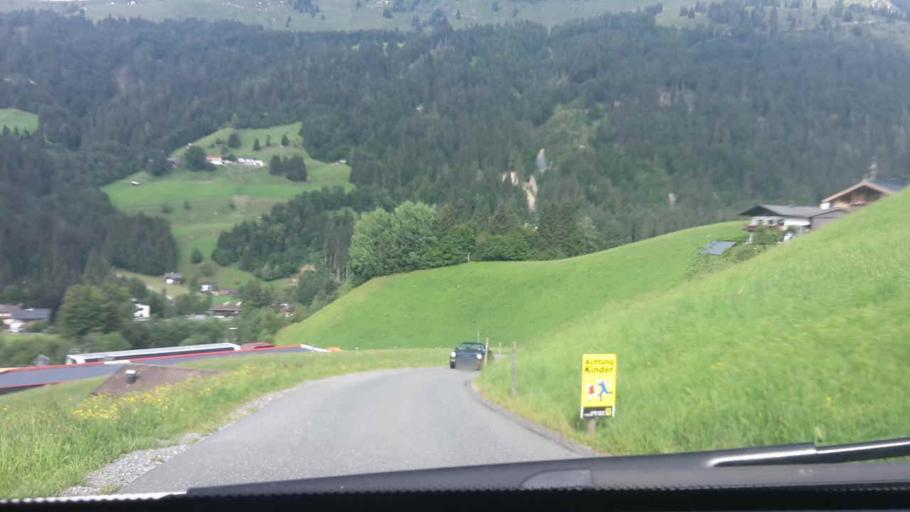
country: AT
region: Tyrol
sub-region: Politischer Bezirk Kitzbuhel
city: Kirchberg in Tirol
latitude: 47.4173
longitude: 12.3176
